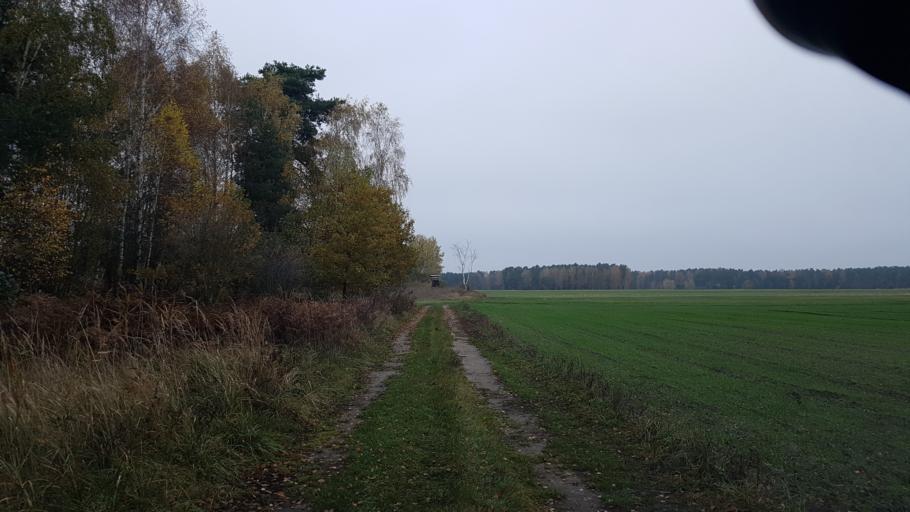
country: DE
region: Brandenburg
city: Ruckersdorf
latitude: 51.5695
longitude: 13.6459
